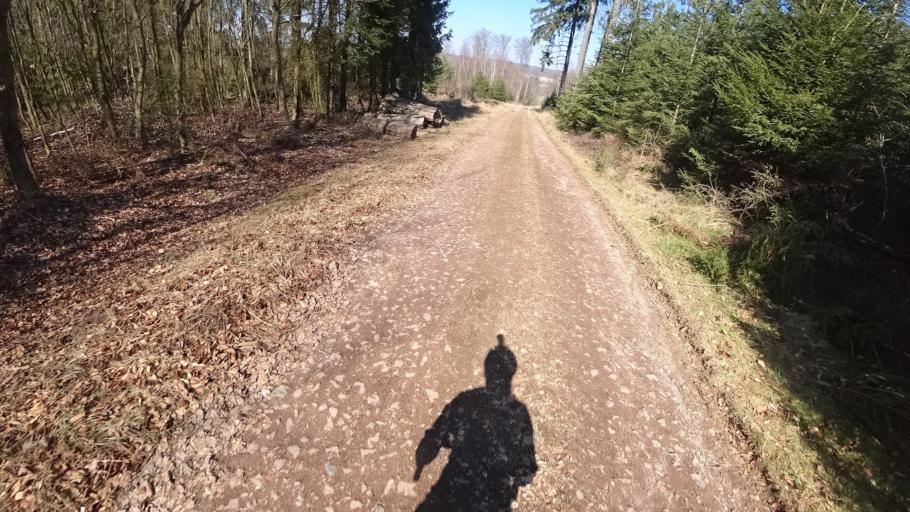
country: DE
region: Rheinland-Pfalz
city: Steinbach
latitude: 50.0342
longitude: 7.5896
